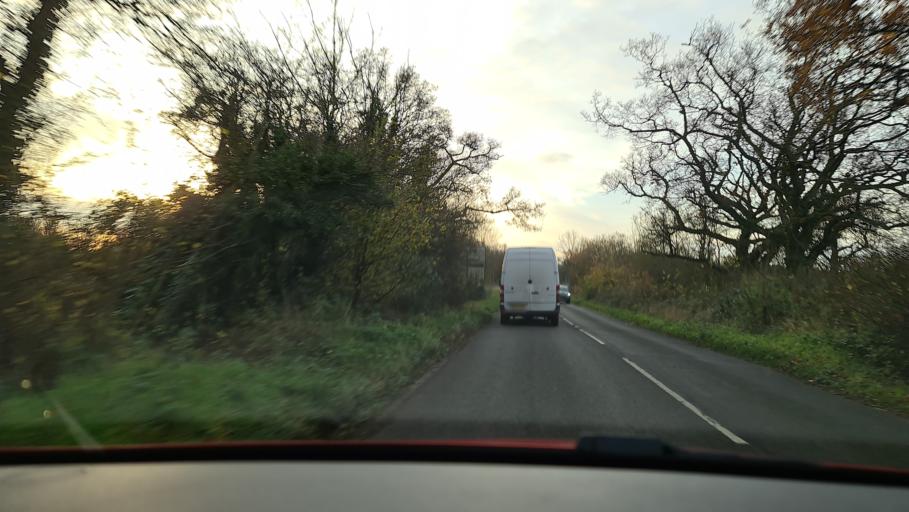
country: GB
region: England
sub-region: Oxfordshire
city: Kidlington
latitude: 51.8414
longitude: -1.2471
